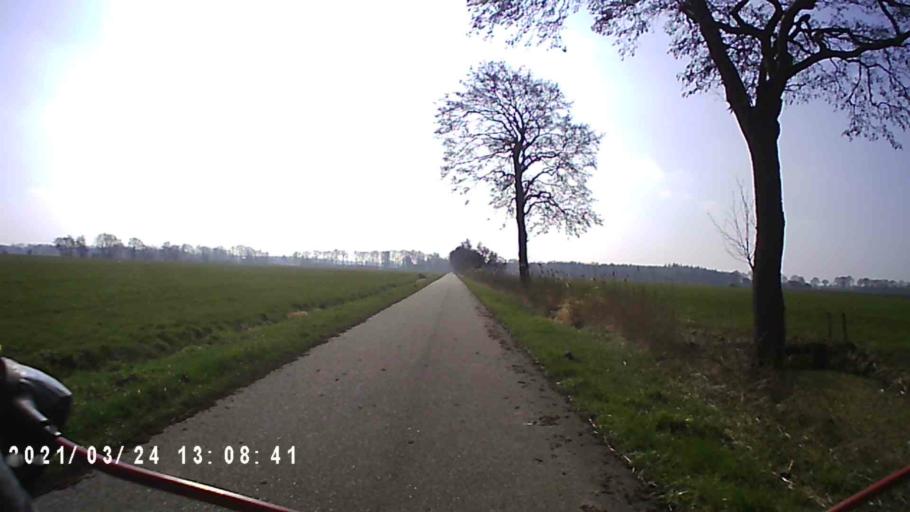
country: NL
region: Groningen
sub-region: Gemeente Leek
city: Leek
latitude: 53.1262
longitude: 6.3038
